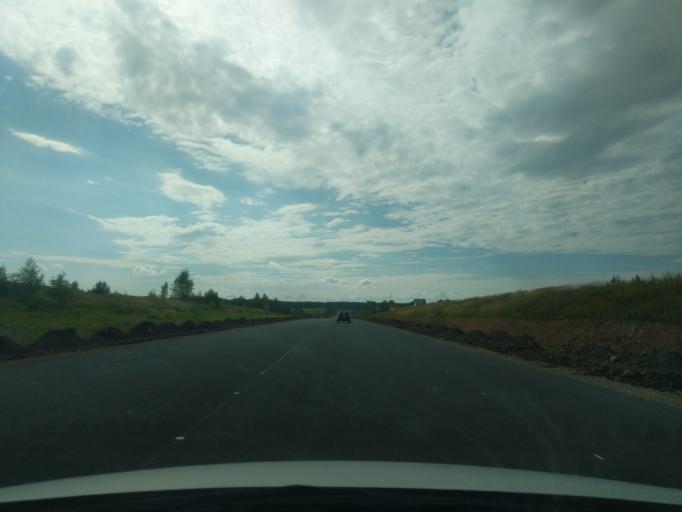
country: RU
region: Kostroma
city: Sudislavl'
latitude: 57.8117
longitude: 41.4694
